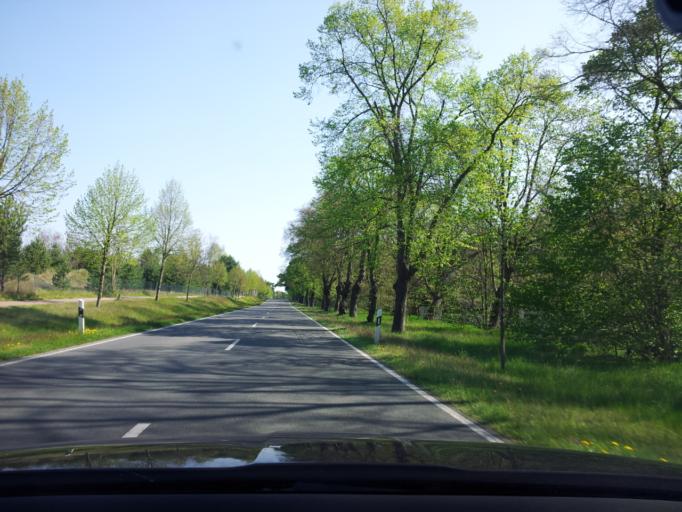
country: DE
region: Brandenburg
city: Juterbog
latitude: 52.0059
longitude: 13.0616
